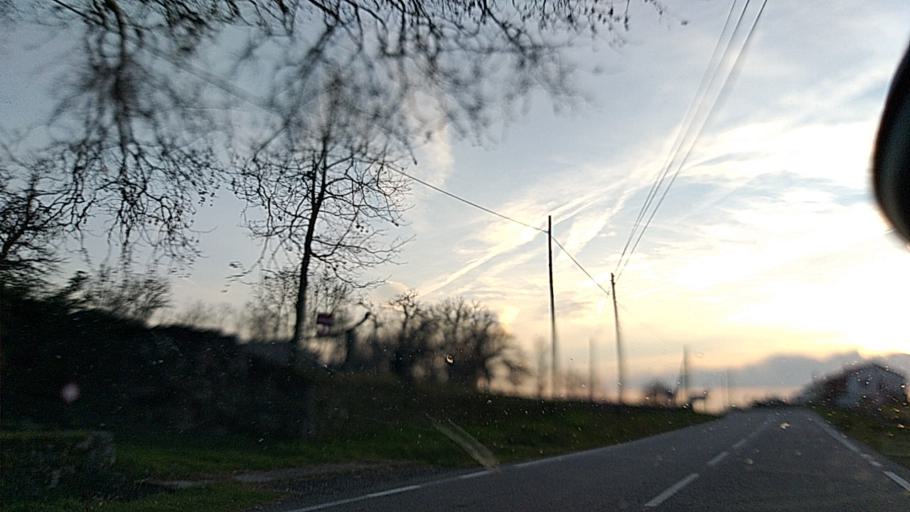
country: PT
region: Guarda
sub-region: Guarda
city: Sequeira
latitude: 40.5936
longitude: -7.1365
